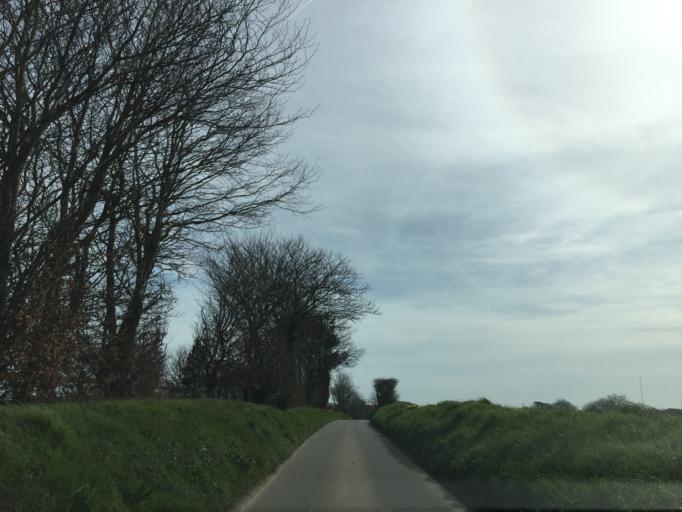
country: JE
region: St Helier
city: Saint Helier
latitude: 49.2279
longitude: -2.1277
